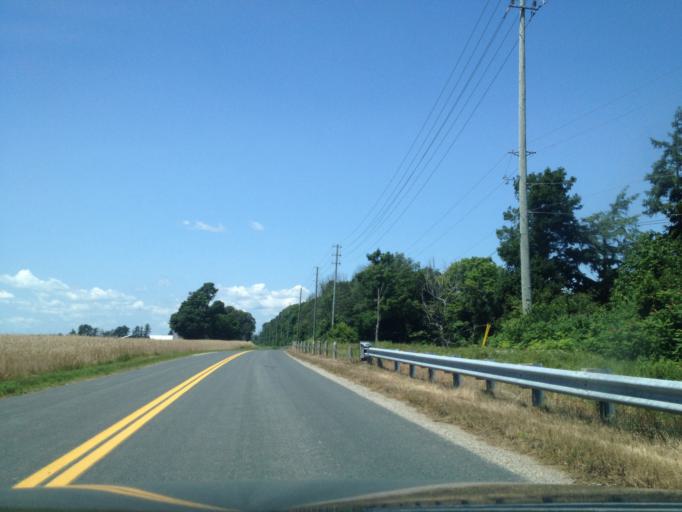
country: CA
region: Ontario
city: Aylmer
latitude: 42.6487
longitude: -80.7610
